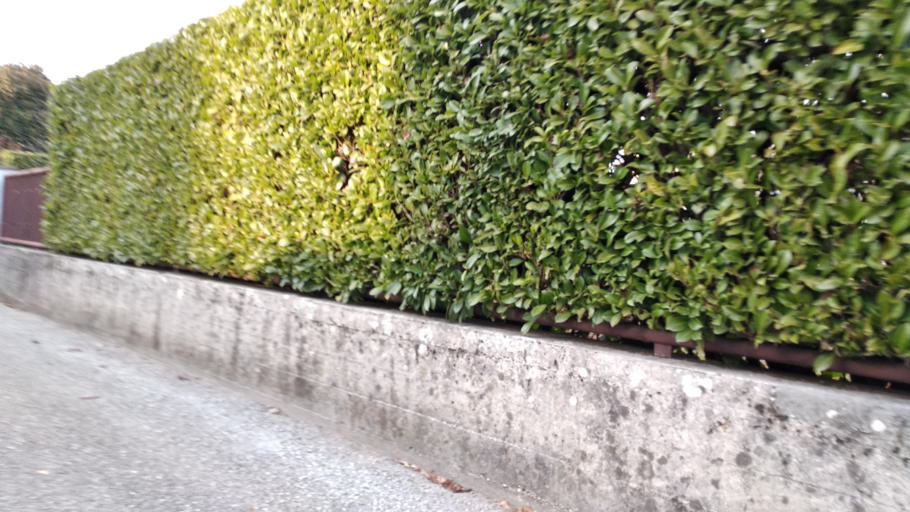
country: IT
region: Veneto
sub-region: Provincia di Vicenza
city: Schio
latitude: 45.7017
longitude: 11.3525
